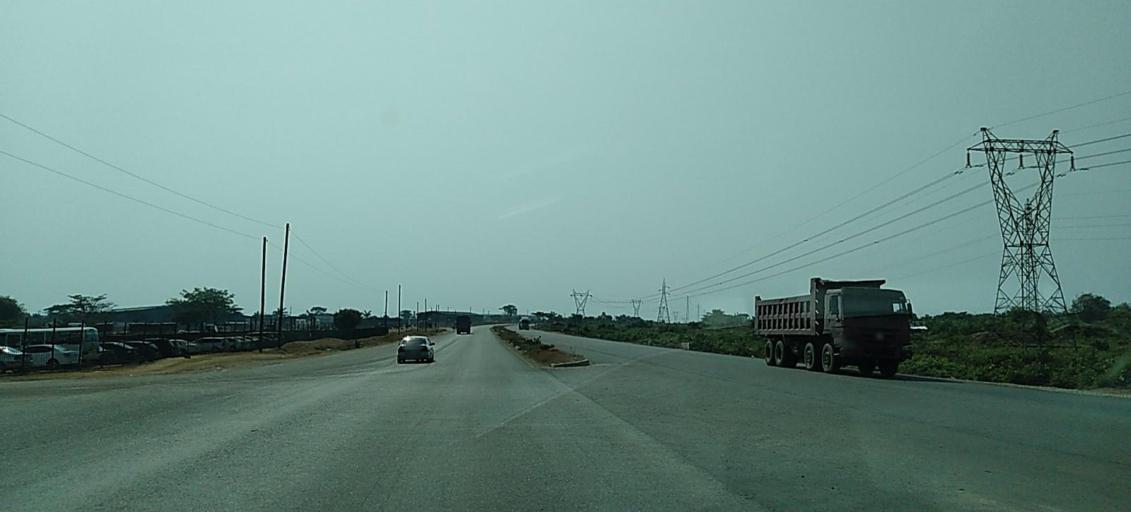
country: ZM
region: Copperbelt
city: Chingola
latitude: -12.5680
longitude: 27.9025
